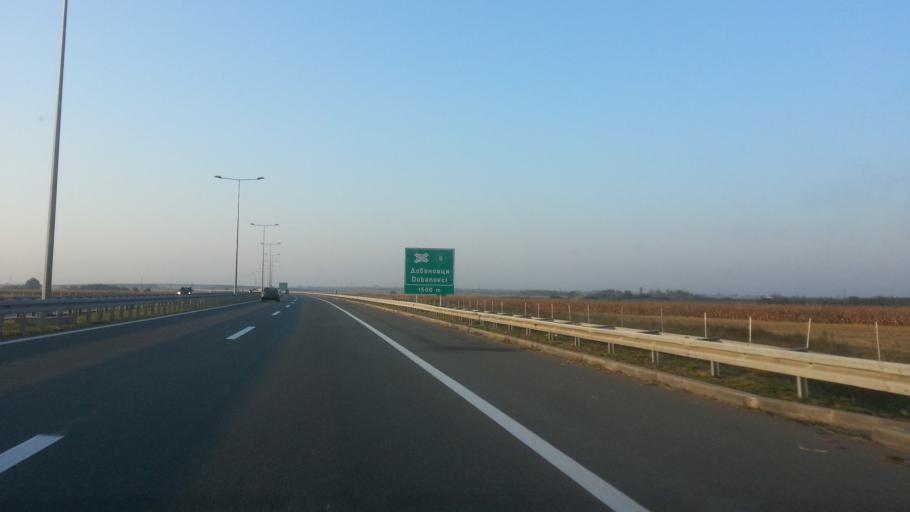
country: RS
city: Dobanovci
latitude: 44.8568
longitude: 20.2497
